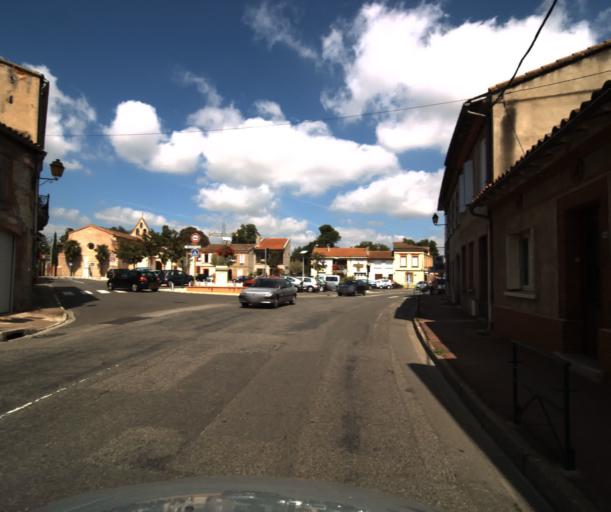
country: FR
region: Midi-Pyrenees
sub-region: Departement de la Haute-Garonne
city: Pinsaguel
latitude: 43.5097
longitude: 1.3890
